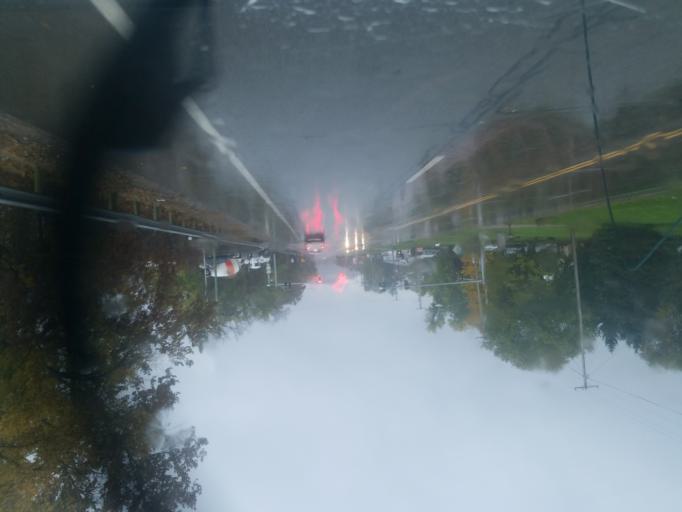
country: US
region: Ohio
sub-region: Muskingum County
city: South Zanesville
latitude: 39.9114
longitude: -82.0015
